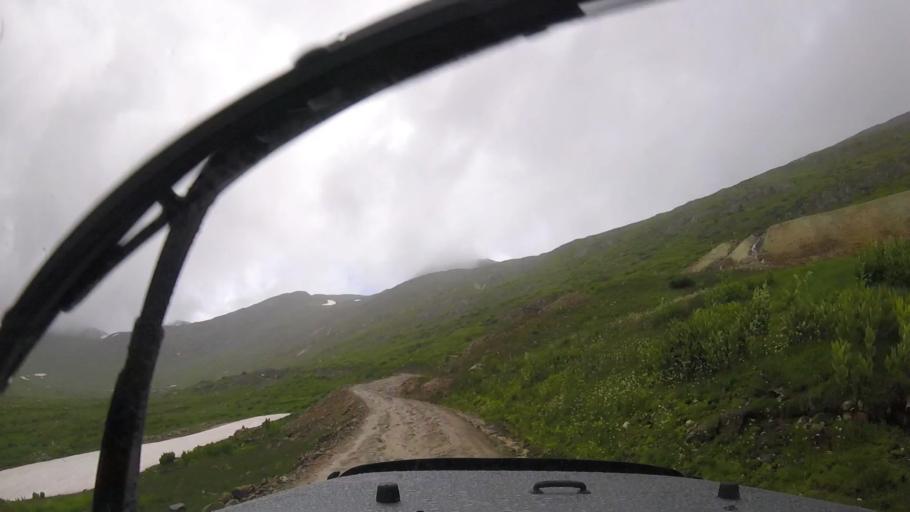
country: US
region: Colorado
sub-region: Ouray County
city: Ouray
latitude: 37.9332
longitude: -107.5968
